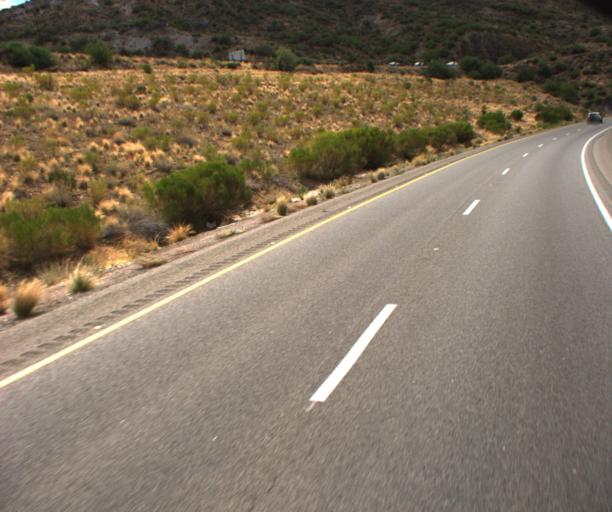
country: US
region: Arizona
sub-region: Yavapai County
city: Black Canyon City
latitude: 34.1243
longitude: -112.1476
